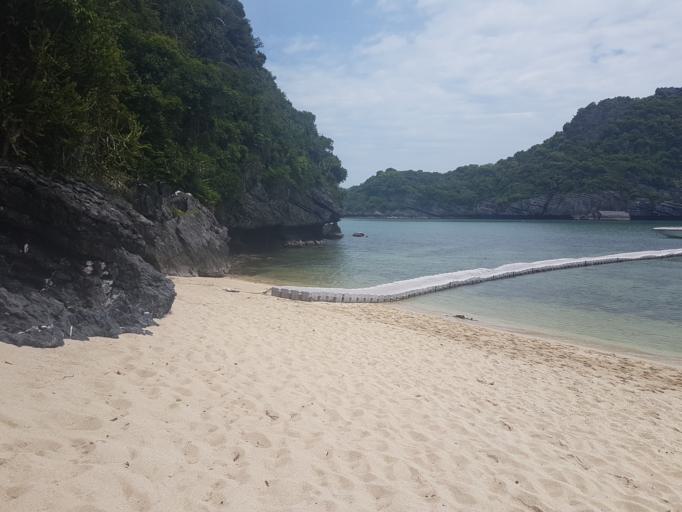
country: TH
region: Surat Thani
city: Ko Samui
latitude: 9.6636
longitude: 99.6799
